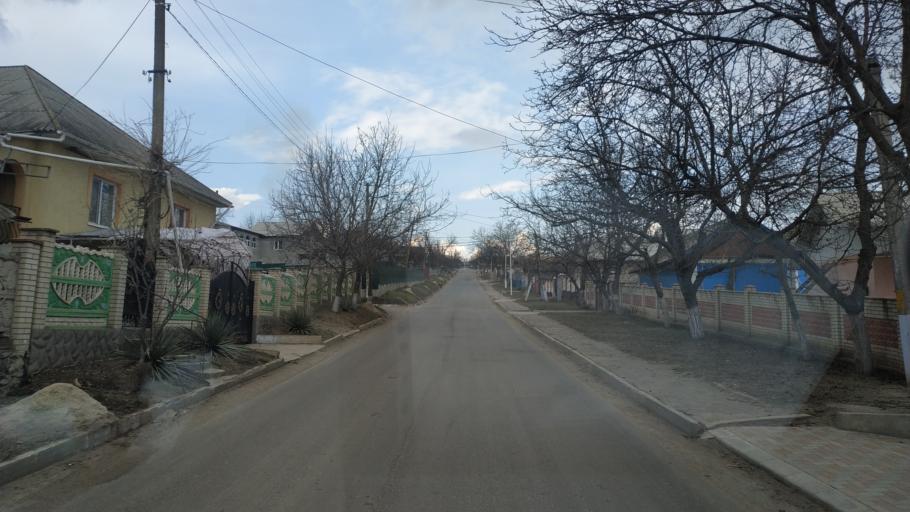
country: MD
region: Anenii Noi
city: Varnita
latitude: 46.8448
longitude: 29.3575
